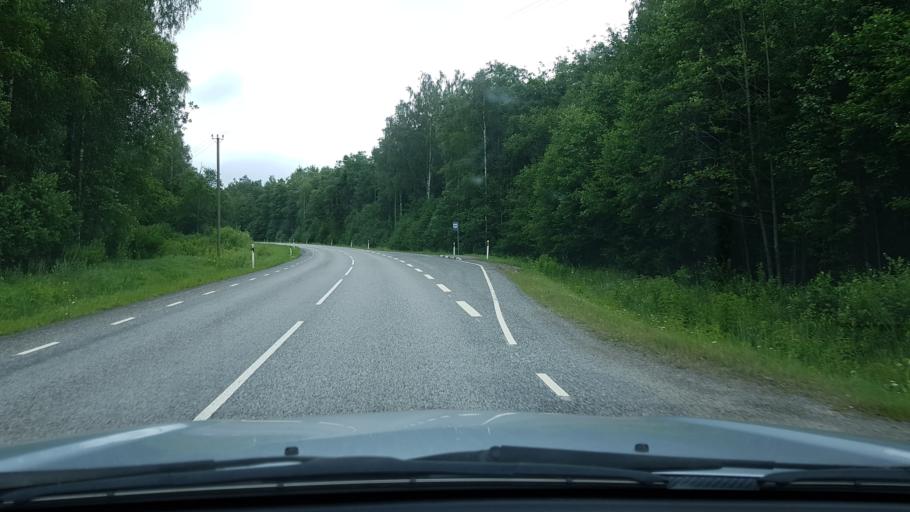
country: EE
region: Ida-Virumaa
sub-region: Narva-Joesuu linn
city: Narva-Joesuu
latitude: 59.3578
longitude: 27.9271
